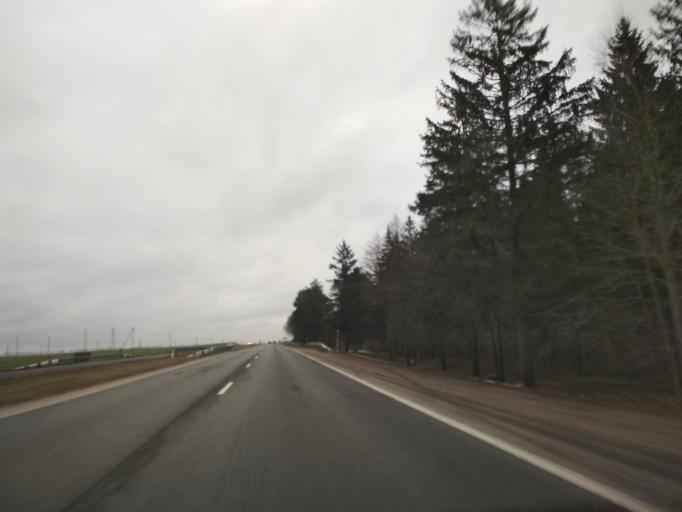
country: BY
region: Minsk
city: Mar''ina Horka
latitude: 53.6090
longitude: 28.0692
